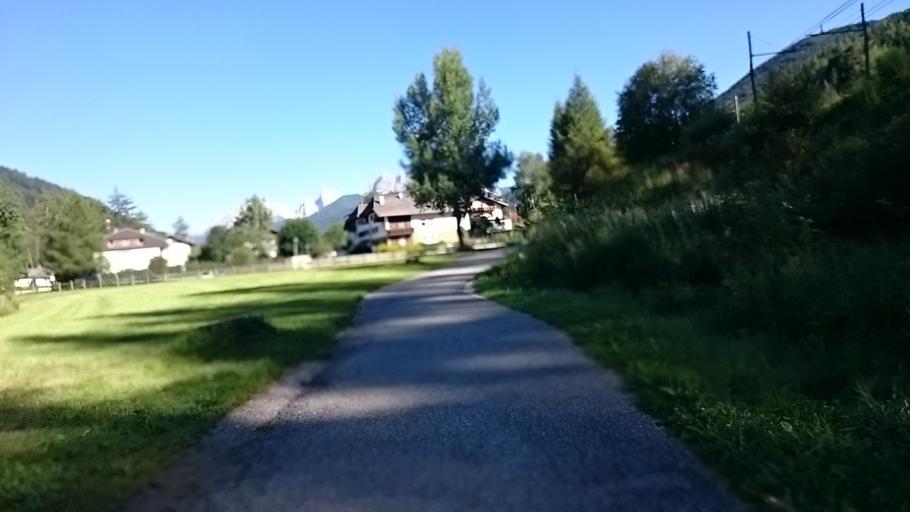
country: IT
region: Trentino-Alto Adige
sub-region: Bolzano
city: Monguelfo
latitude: 46.7551
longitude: 12.1027
